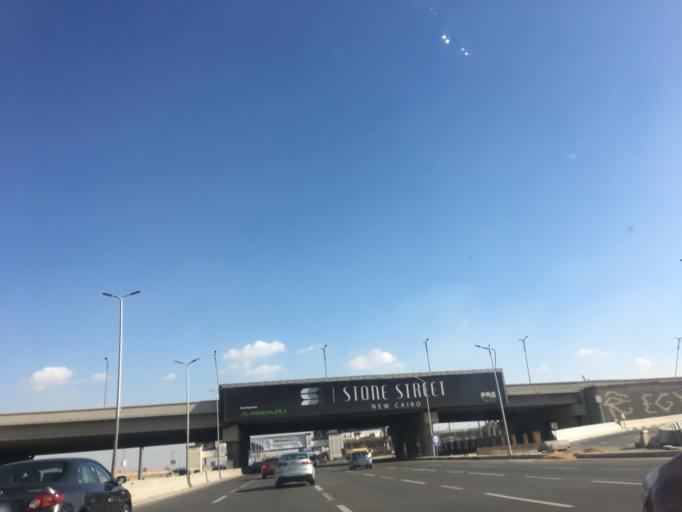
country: EG
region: Muhafazat al Qahirah
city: Cairo
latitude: 30.0228
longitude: 31.3686
